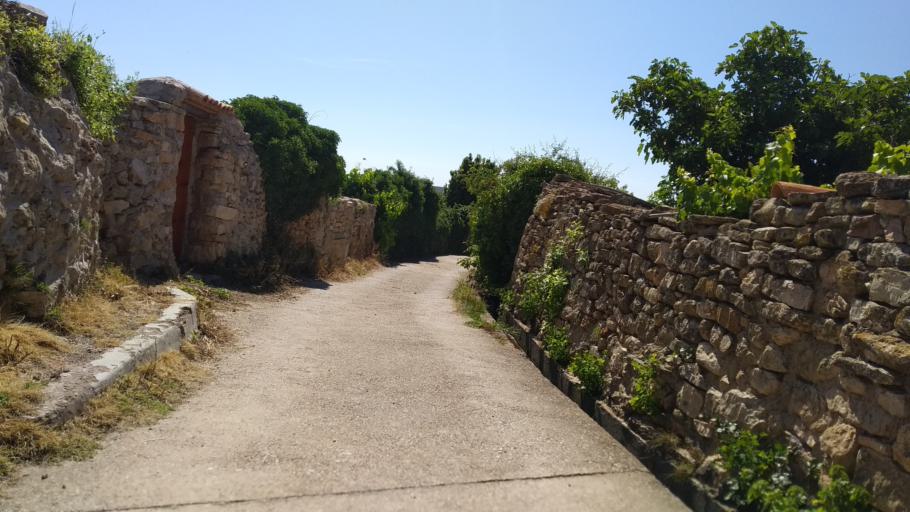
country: ES
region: Aragon
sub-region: Provincia de Teruel
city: Monforte de Moyuela
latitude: 41.0527
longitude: -1.0140
